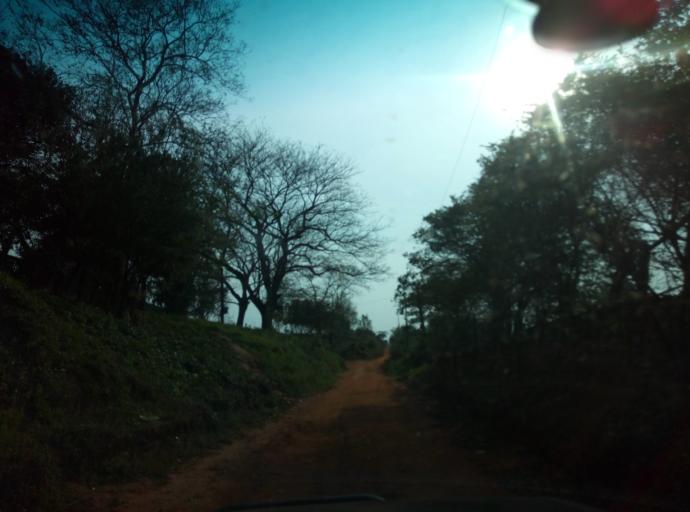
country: PY
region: Caaguazu
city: San Joaquin
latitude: -25.1499
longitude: -56.1019
